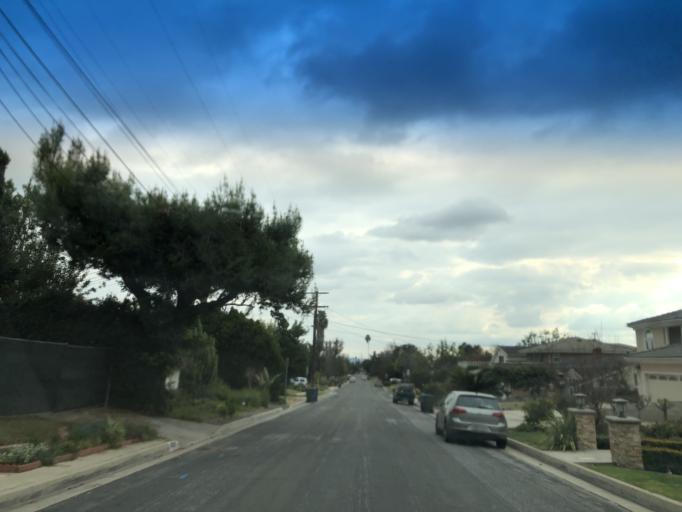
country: US
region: California
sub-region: Los Angeles County
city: San Marino
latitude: 34.1255
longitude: -118.0871
